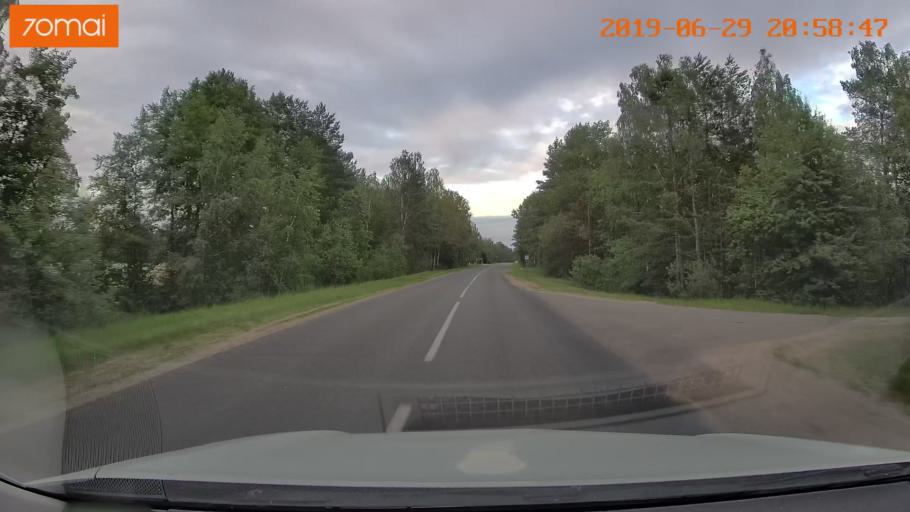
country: BY
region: Brest
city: Hantsavichy
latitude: 52.7328
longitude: 26.3929
